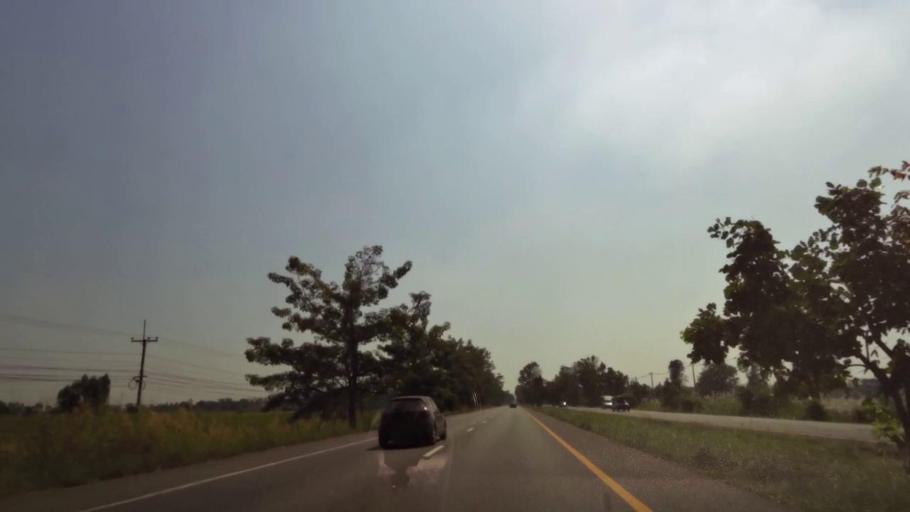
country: TH
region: Nakhon Sawan
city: Banphot Phisai
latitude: 16.0077
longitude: 100.1155
